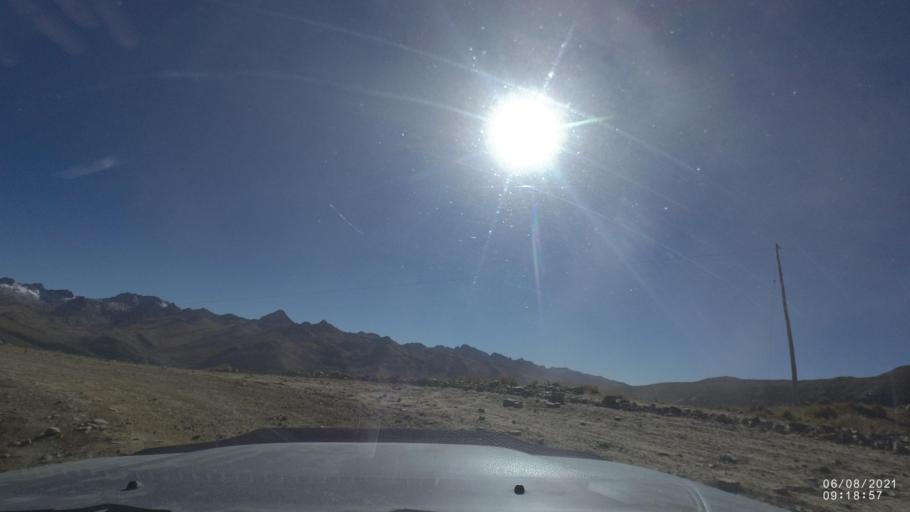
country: BO
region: Cochabamba
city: Colchani
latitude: -17.0326
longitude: -66.5309
